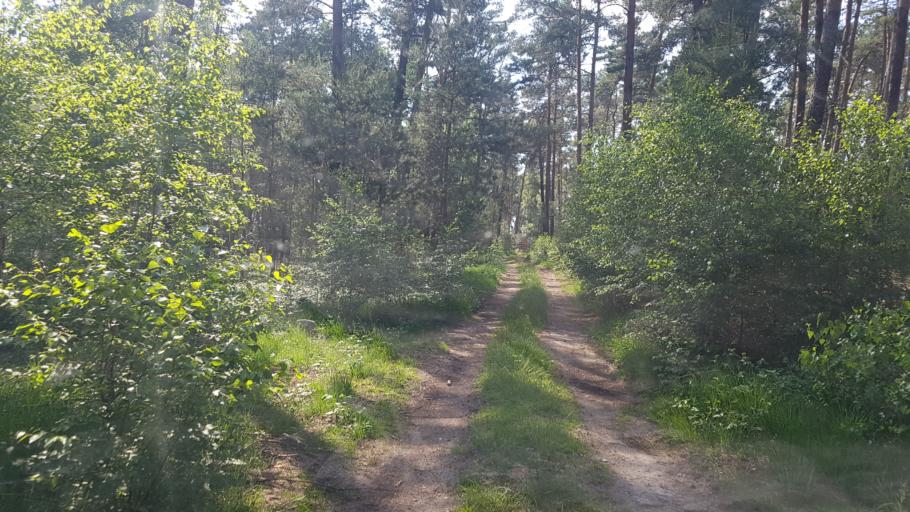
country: DE
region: Brandenburg
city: Trobitz
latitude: 51.6398
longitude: 13.4193
